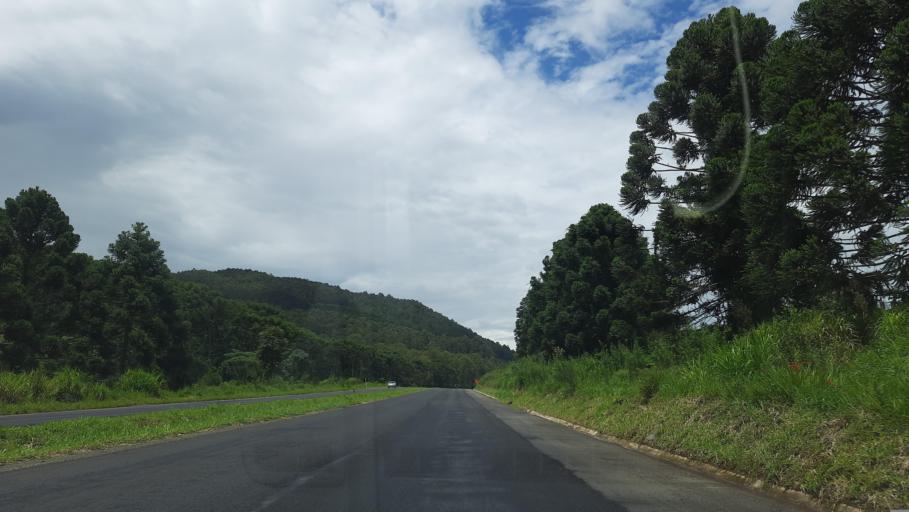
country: BR
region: Minas Gerais
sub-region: Pocos De Caldas
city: Pocos de Caldas
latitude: -21.8075
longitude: -46.6539
